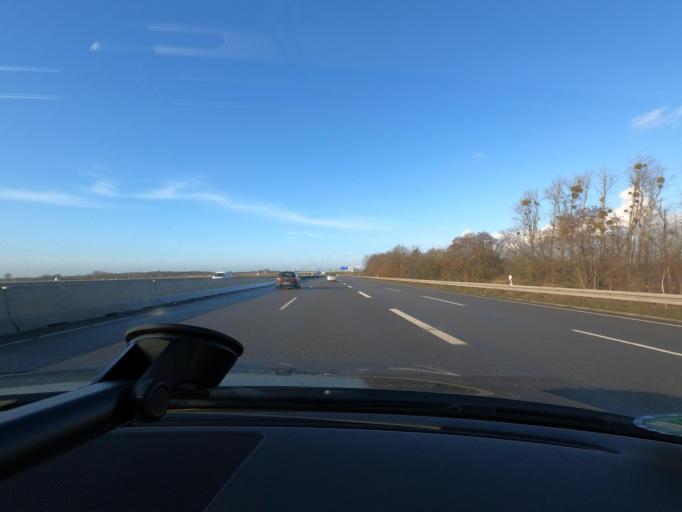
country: DE
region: North Rhine-Westphalia
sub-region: Regierungsbezirk Dusseldorf
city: Hochfeld
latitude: 51.3521
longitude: 6.7681
